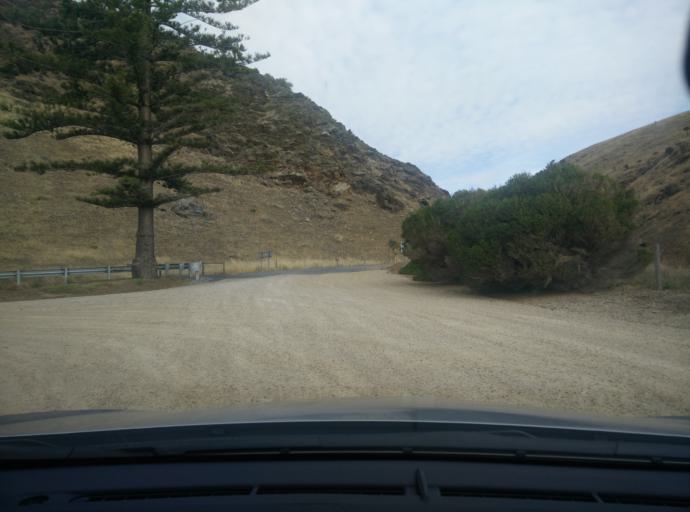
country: AU
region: South Australia
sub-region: Yankalilla
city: Normanville
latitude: -35.4813
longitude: 138.2750
